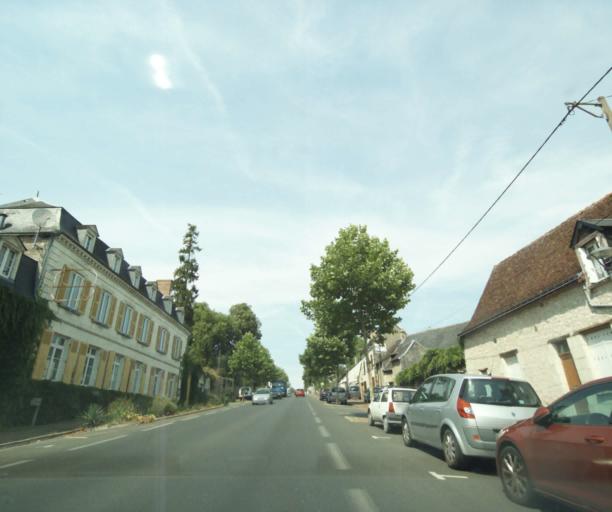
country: FR
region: Centre
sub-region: Departement d'Indre-et-Loire
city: Sainte-Maure-de-Touraine
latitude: 47.1157
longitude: 0.6189
